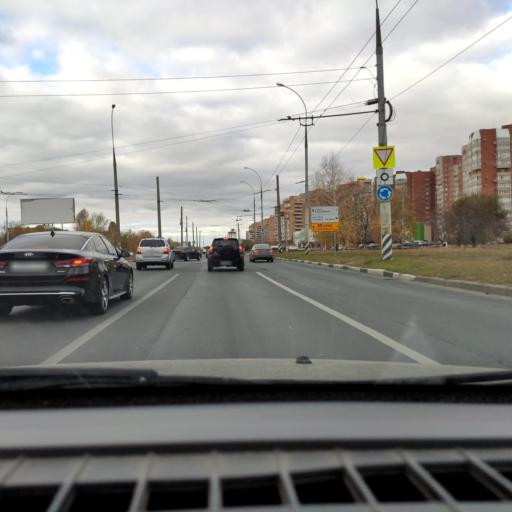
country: RU
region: Samara
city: Tol'yatti
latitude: 53.4988
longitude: 49.2924
